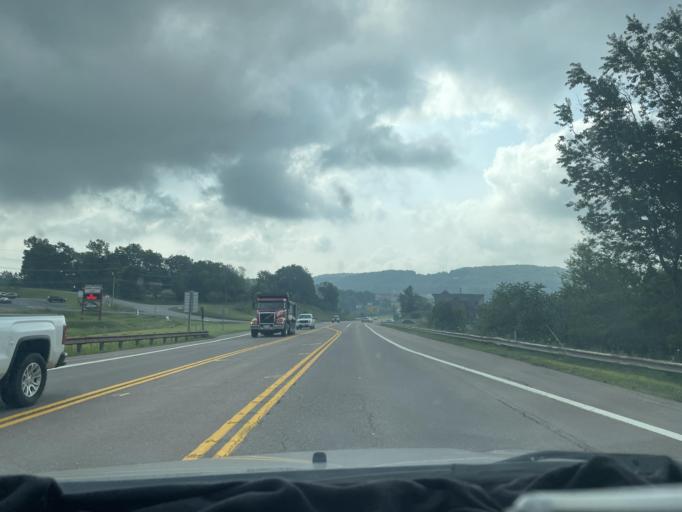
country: US
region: Maryland
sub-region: Garrett County
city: Oakland
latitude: 39.5620
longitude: -79.3582
